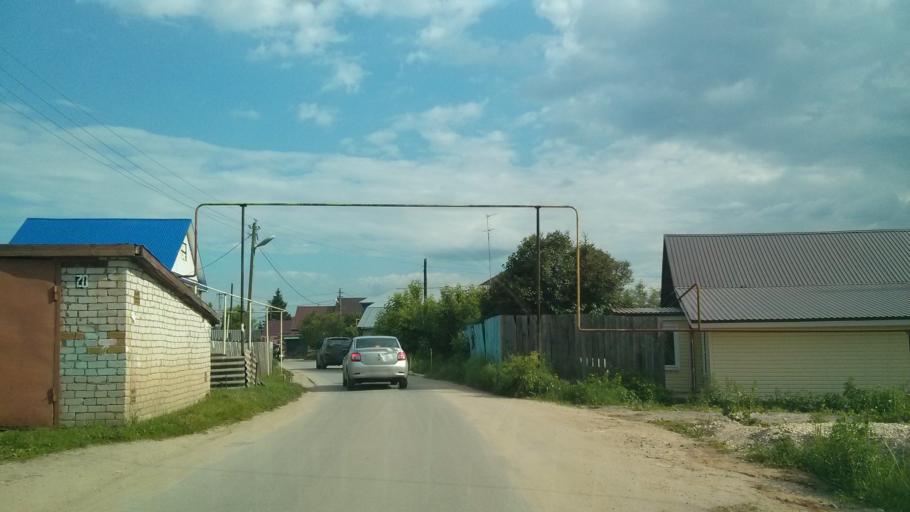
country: RU
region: Nizjnij Novgorod
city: Afonino
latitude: 56.2798
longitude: 44.1028
